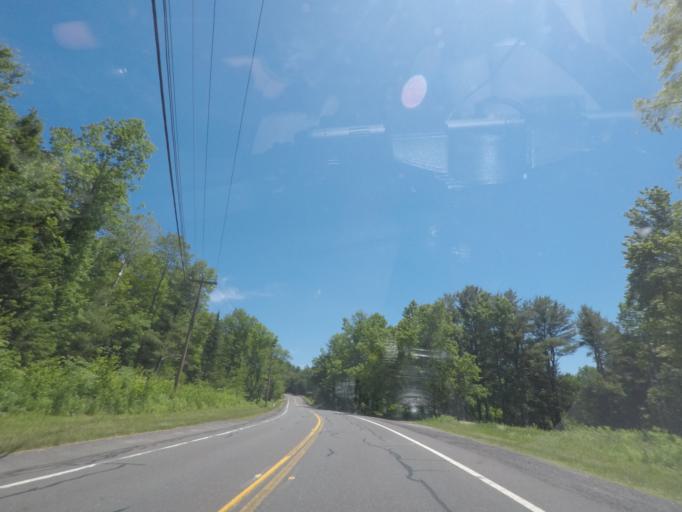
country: US
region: Massachusetts
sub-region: Berkshire County
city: Otis
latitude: 42.2539
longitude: -73.1154
